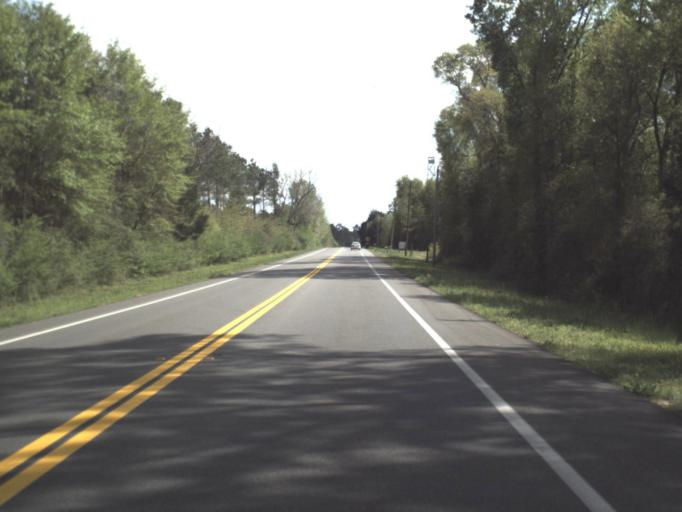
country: US
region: Alabama
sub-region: Covington County
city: Florala
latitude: 30.9406
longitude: -86.4788
